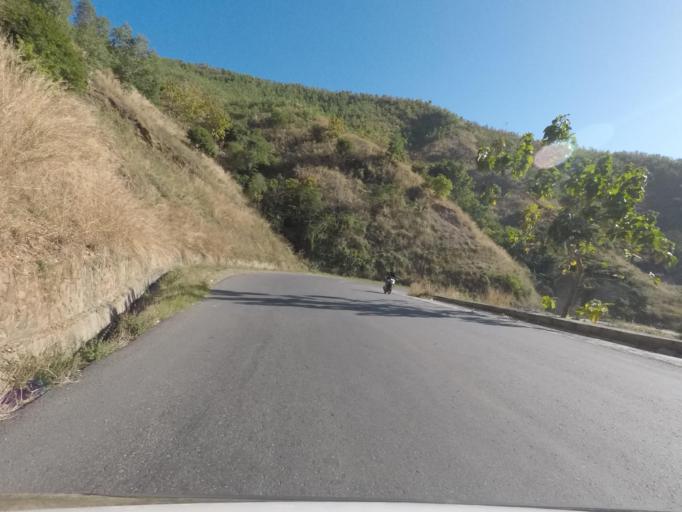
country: TL
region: Dili
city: Dili
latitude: -8.5621
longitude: 125.6345
